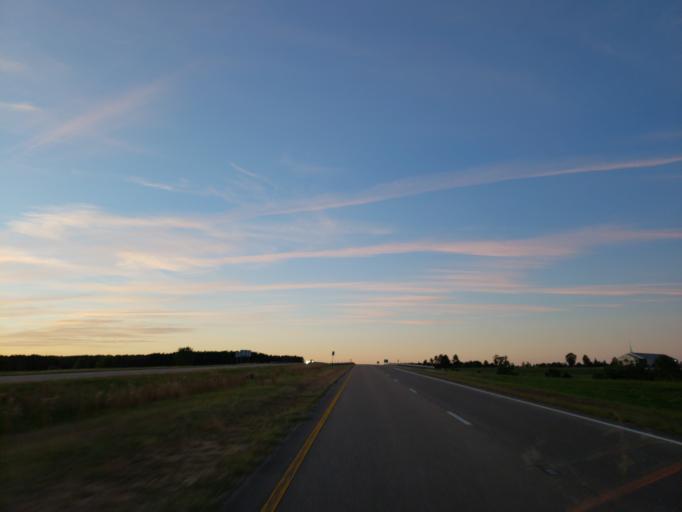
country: US
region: Mississippi
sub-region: Wayne County
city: Waynesboro
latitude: 31.7059
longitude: -88.6248
